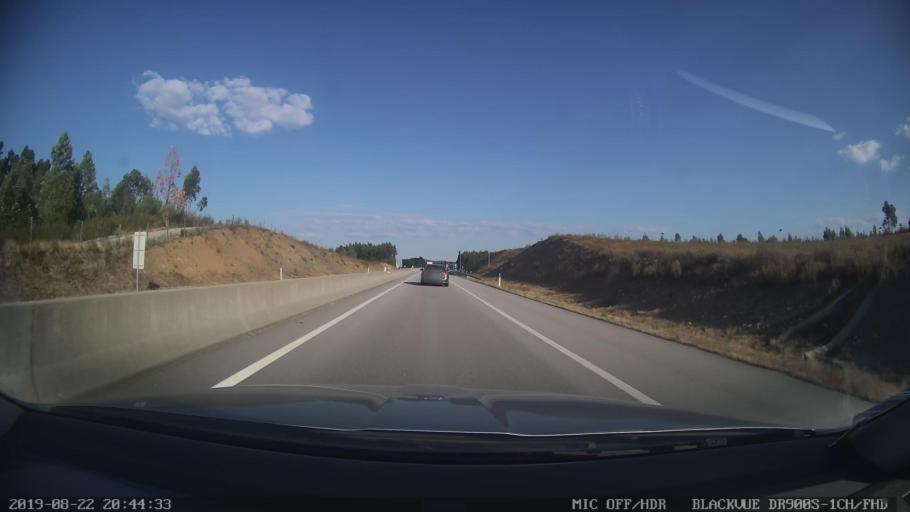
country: PT
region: Castelo Branco
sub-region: Proenca-A-Nova
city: Proenca-a-Nova
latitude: 39.7085
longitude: -7.8535
